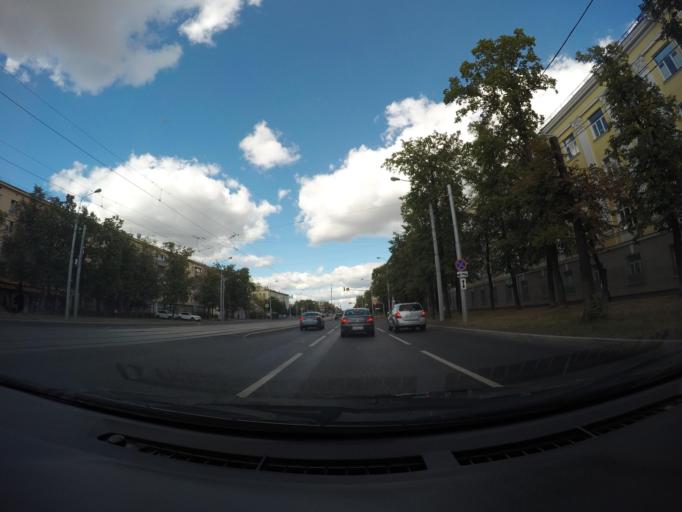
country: RU
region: Moscow
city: Lefortovo
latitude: 55.7666
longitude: 37.7315
